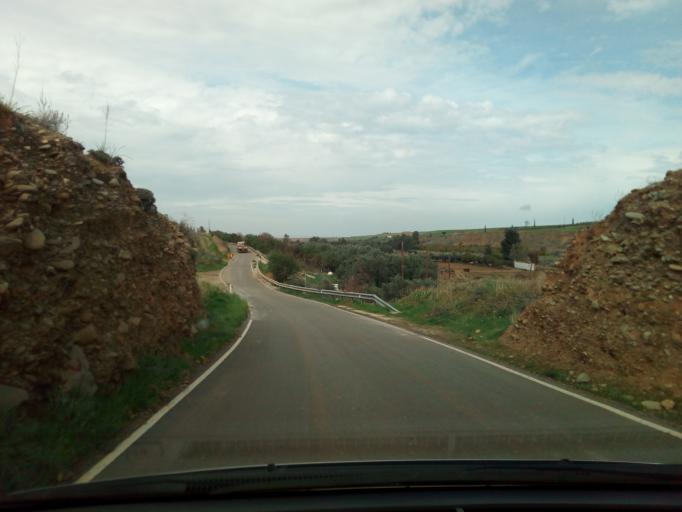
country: CY
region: Lefkosia
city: Astromeritis
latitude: 35.0998
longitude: 32.9831
